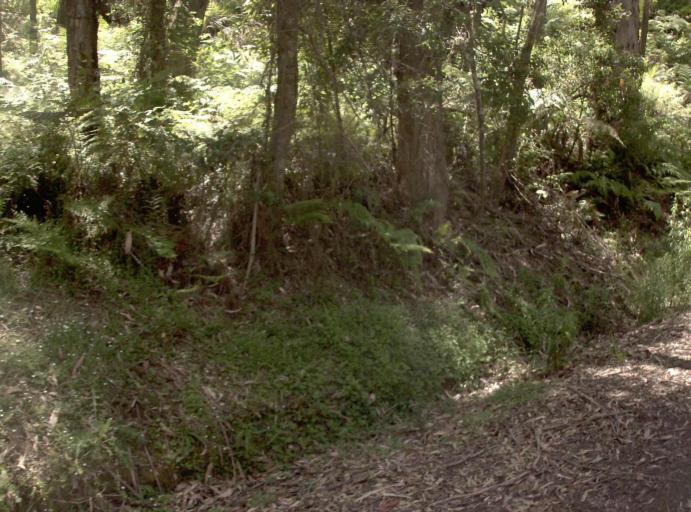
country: AU
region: New South Wales
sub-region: Bombala
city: Bombala
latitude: -37.4647
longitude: 148.9354
